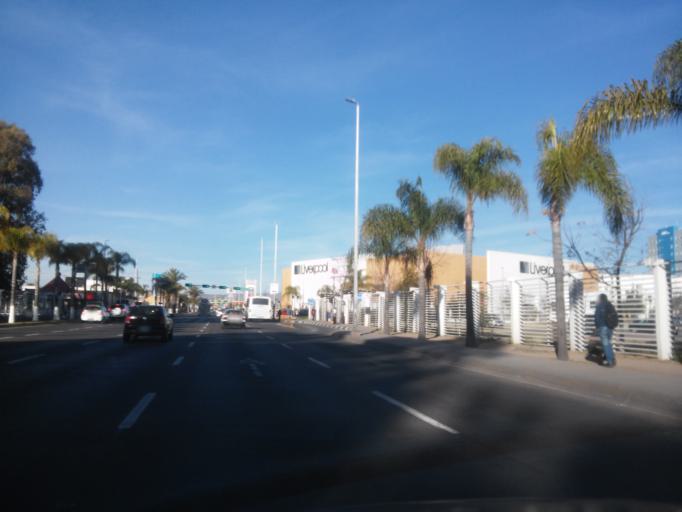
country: MX
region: Durango
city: Victoria de Durango
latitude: 24.0343
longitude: -104.6478
